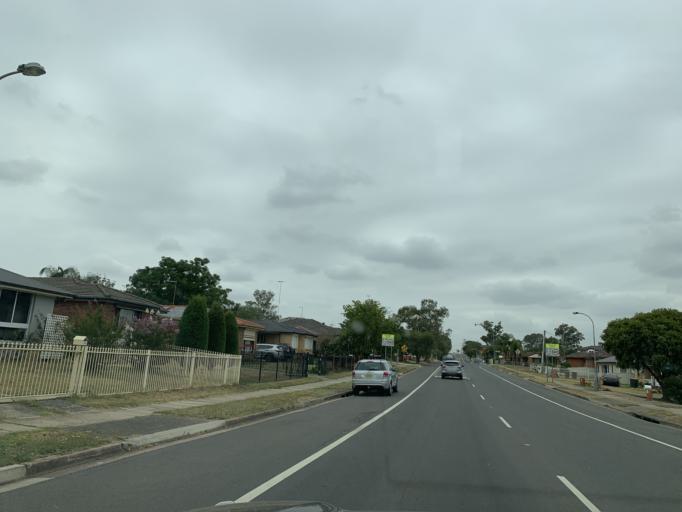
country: AU
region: New South Wales
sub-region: Blacktown
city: Doonside
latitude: -33.7526
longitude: 150.8715
